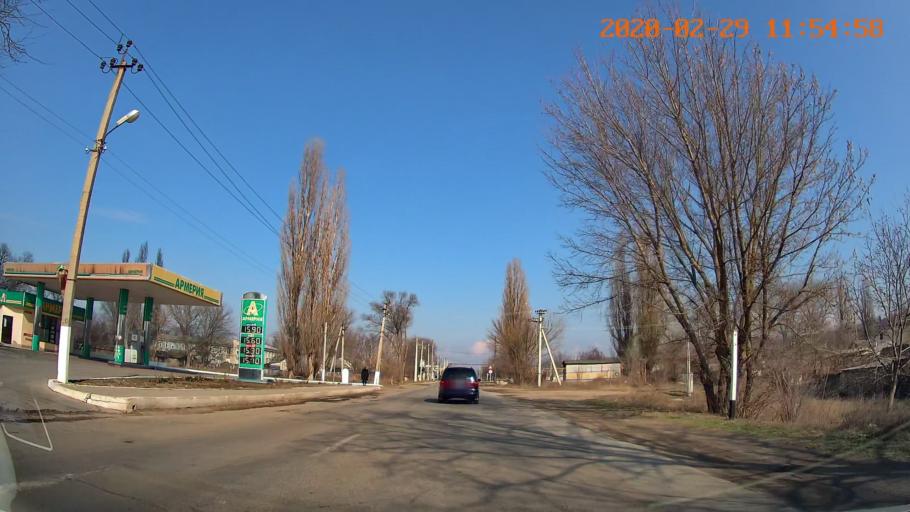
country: MD
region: Telenesti
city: Ribnita
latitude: 47.7873
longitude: 28.9967
